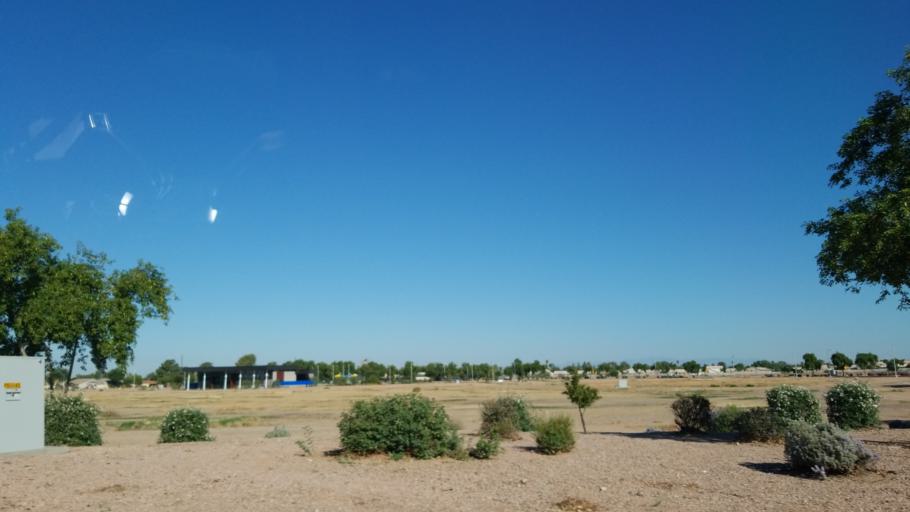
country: US
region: Arizona
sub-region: Maricopa County
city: Glendale
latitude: 33.5235
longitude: -112.2339
